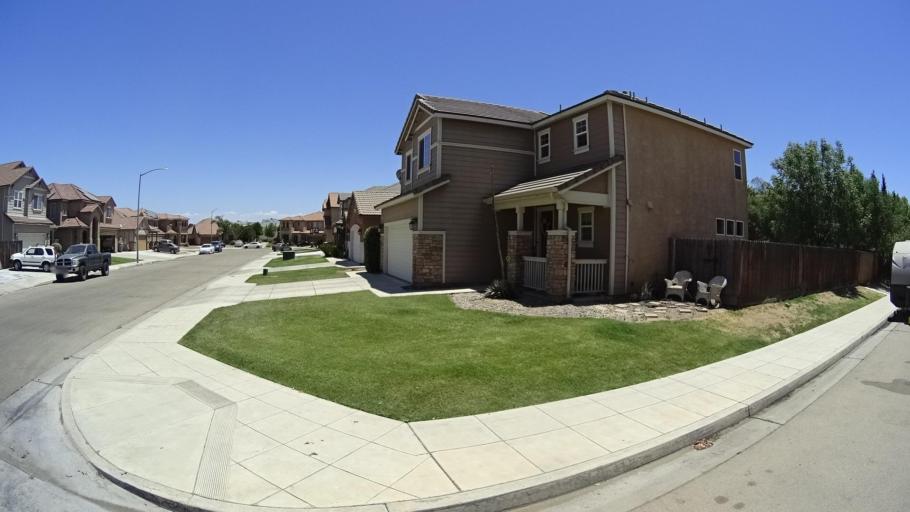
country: US
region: California
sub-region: Fresno County
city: Sunnyside
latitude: 36.7279
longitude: -119.6661
